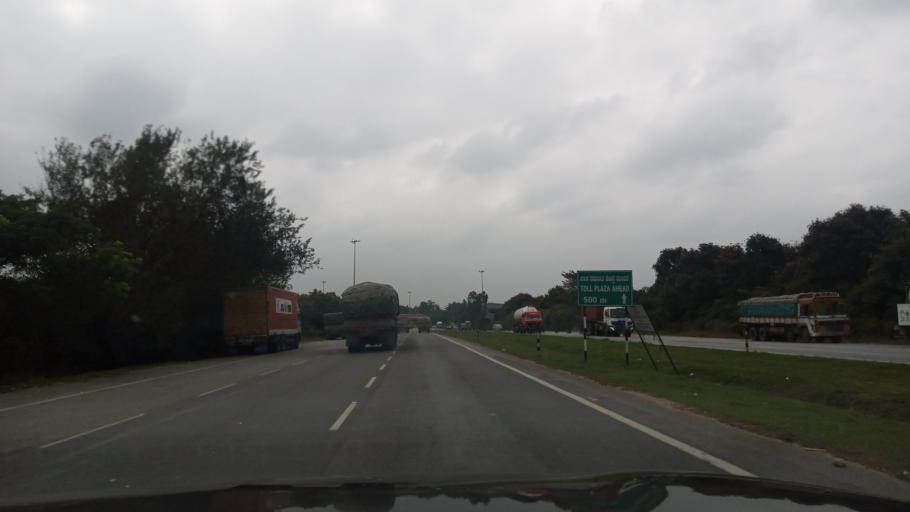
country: IN
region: Karnataka
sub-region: Bangalore Rural
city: Nelamangala
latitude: 13.0471
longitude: 77.4758
